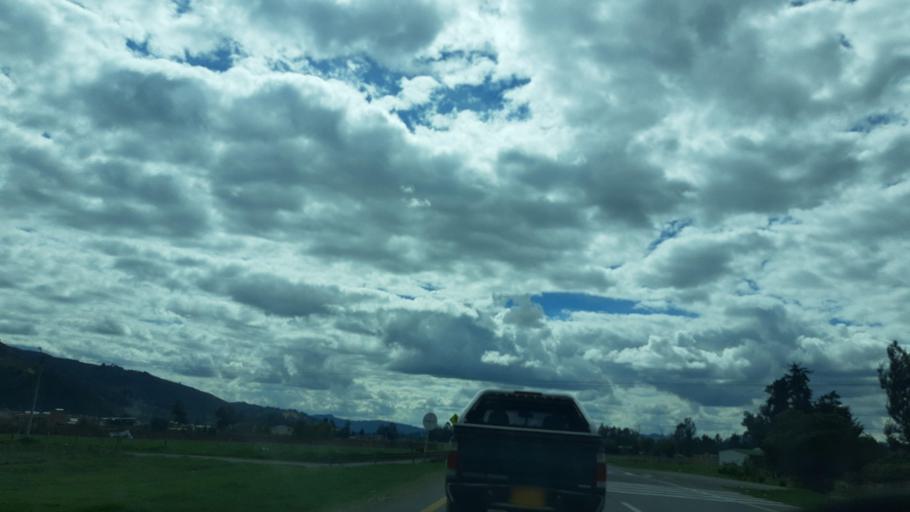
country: CO
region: Cundinamarca
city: Gachancipa
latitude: 4.9997
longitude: -73.8694
